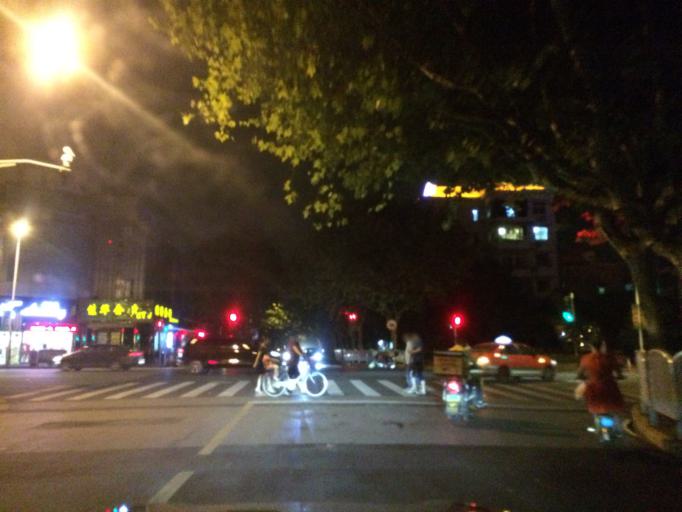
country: CN
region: Shanghai Shi
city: Baoshan
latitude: 31.4062
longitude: 121.4846
